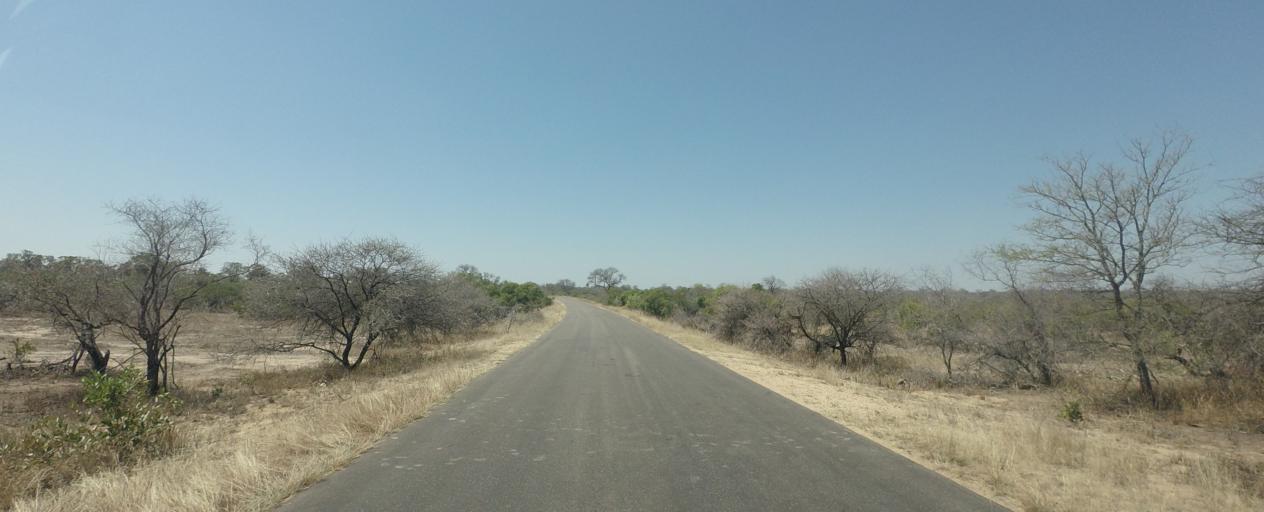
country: ZA
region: Limpopo
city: Thulamahashi
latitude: -24.4234
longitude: 31.5088
